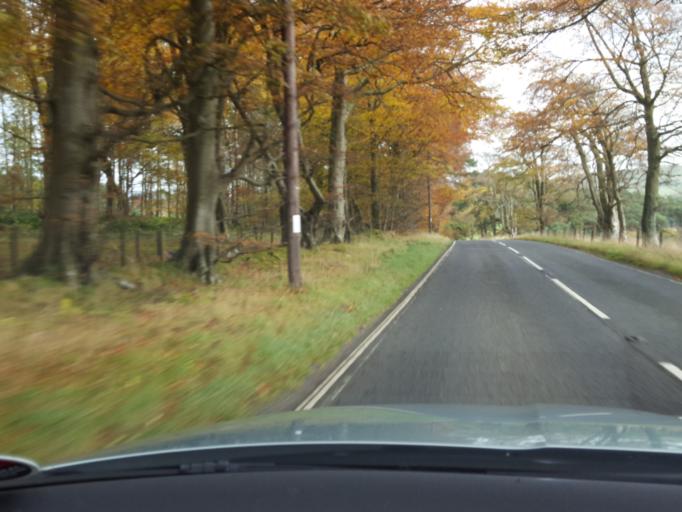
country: GB
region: Scotland
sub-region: The Scottish Borders
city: West Linton
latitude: 55.6844
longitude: -3.4242
